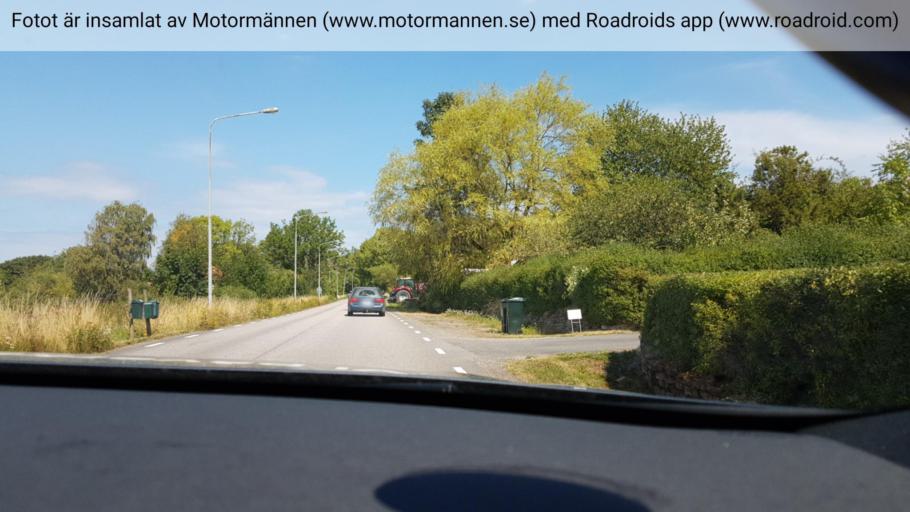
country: SE
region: Vaestra Goetaland
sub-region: Gotene Kommun
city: Kallby
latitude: 58.5620
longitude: 13.3507
